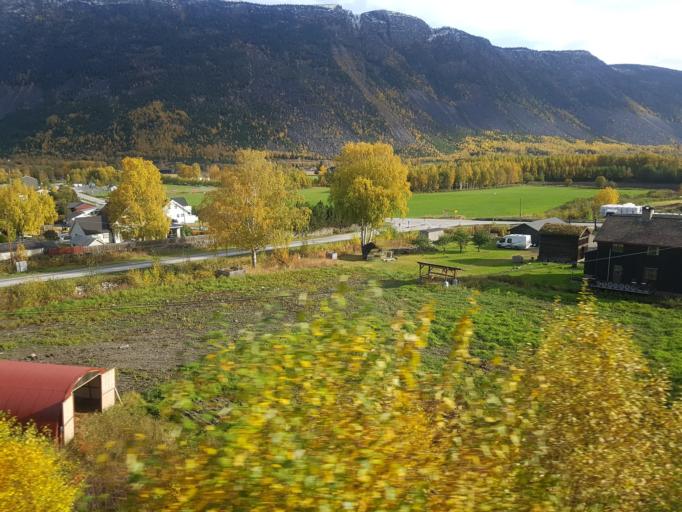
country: NO
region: Oppland
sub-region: Sel
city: Otta
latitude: 61.8411
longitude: 9.4069
